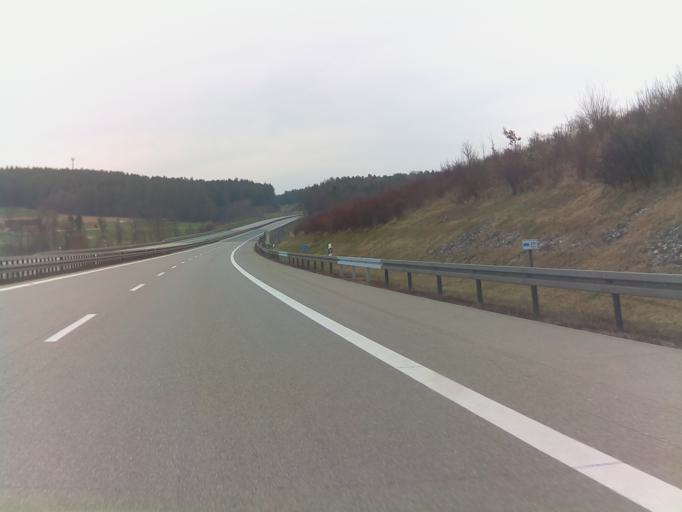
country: DE
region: Bavaria
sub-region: Upper Palatinate
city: Ebermannsdorf
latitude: 49.4227
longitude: 12.0011
